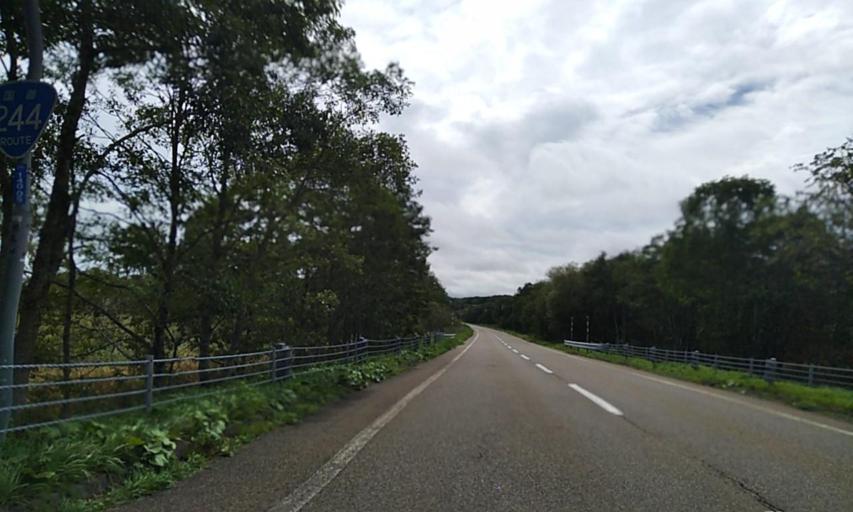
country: JP
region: Hokkaido
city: Shibetsu
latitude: 43.3441
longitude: 145.2148
